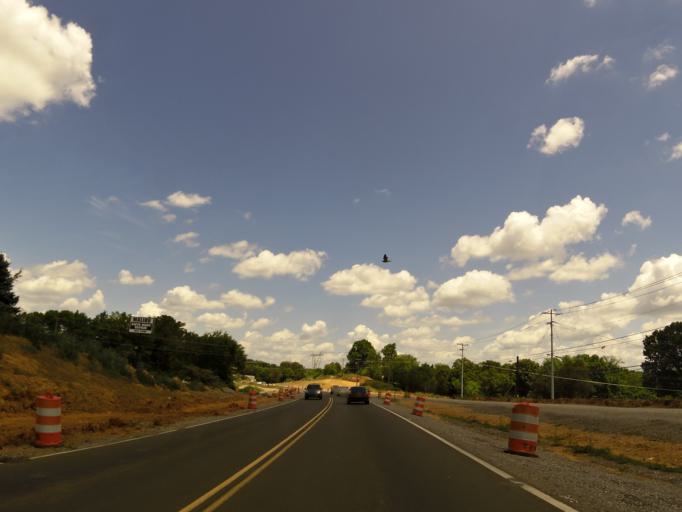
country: US
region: Tennessee
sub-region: Union County
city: Condon
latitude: 36.1018
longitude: -83.9103
